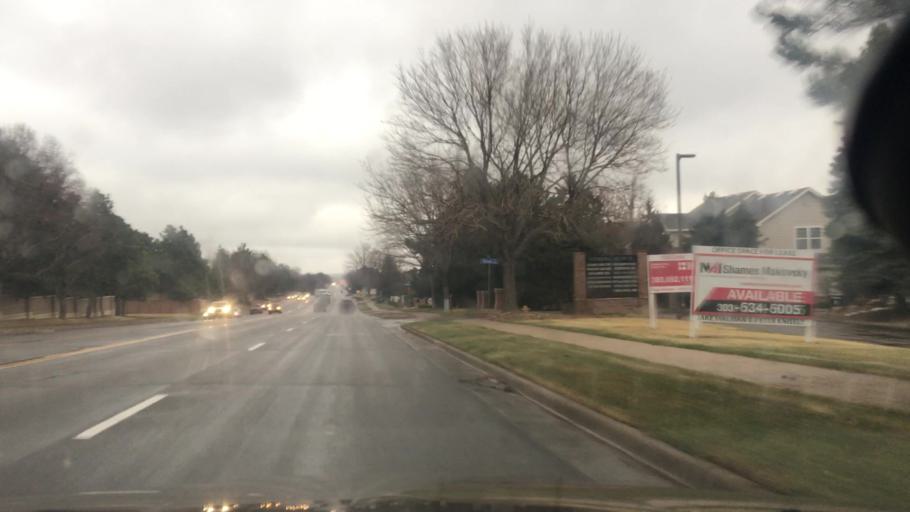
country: US
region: Colorado
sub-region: Arapahoe County
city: Castlewood
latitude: 39.5699
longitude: -104.9230
